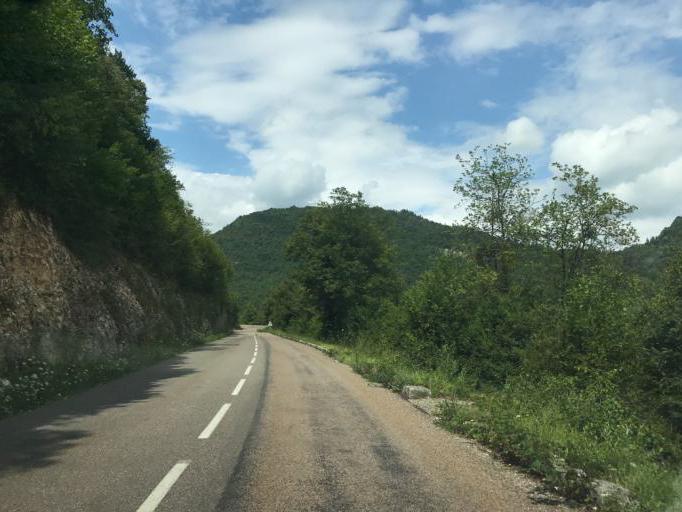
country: FR
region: Franche-Comte
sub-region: Departement du Jura
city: Saint-Claude
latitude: 46.4124
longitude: 5.8665
